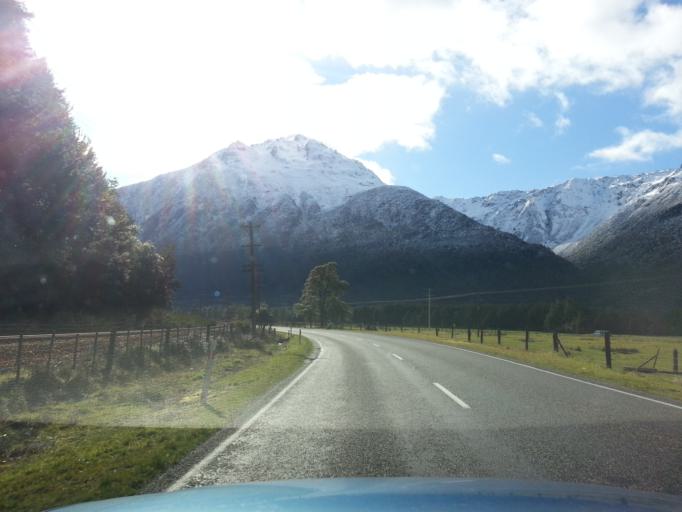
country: NZ
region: West Coast
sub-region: Grey District
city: Greymouth
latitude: -42.7686
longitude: 171.6241
